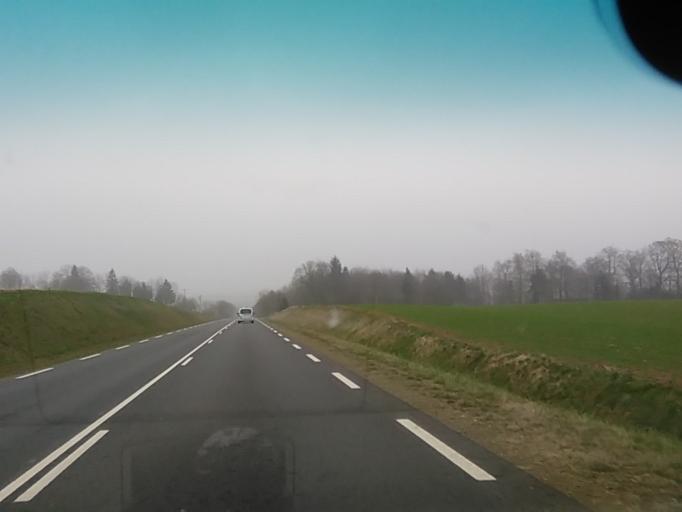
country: FR
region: Lower Normandy
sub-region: Departement de l'Orne
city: Magny-le-Desert
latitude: 48.6187
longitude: -0.2922
